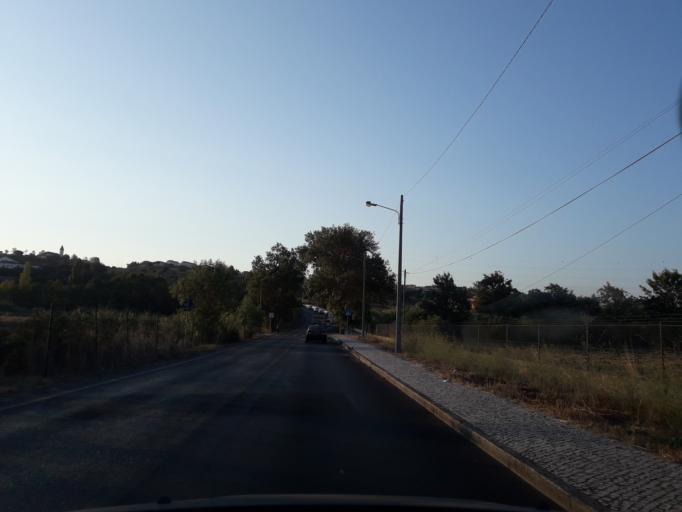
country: PT
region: Lisbon
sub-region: Odivelas
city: Pontinha
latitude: 38.7747
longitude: -9.2049
